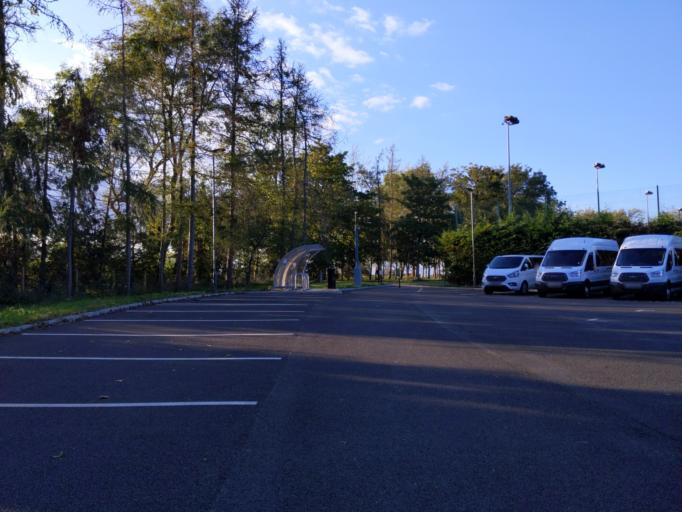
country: GB
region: England
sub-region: Oxfordshire
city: Radley
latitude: 51.6958
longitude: -1.2467
